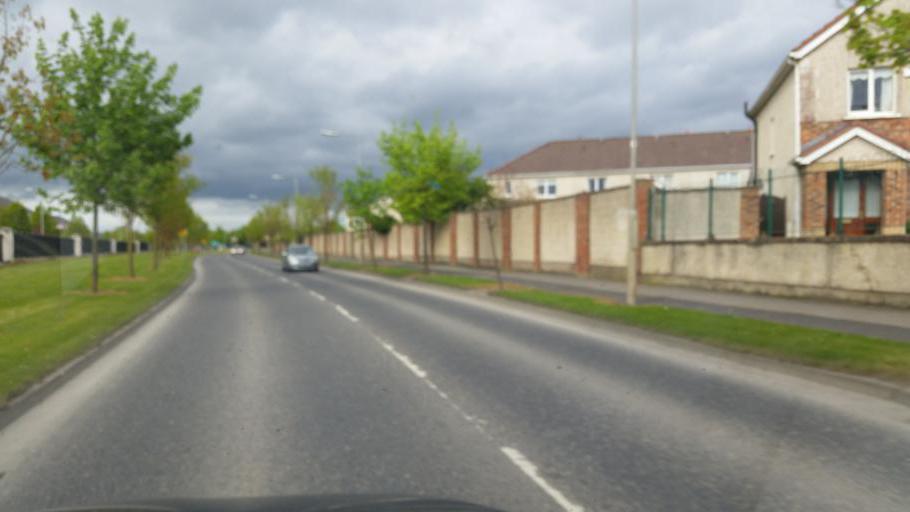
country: IE
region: Leinster
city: Hartstown
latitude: 53.4008
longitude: -6.4381
